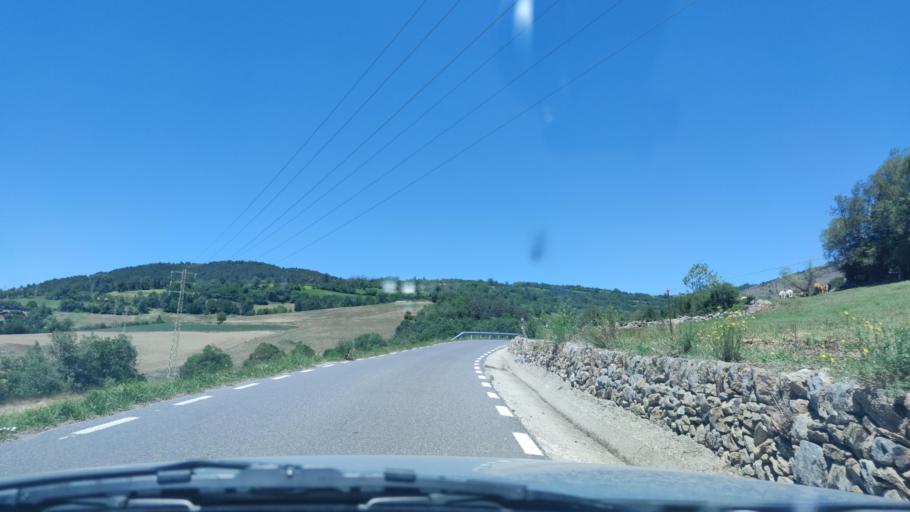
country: ES
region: Catalonia
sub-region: Provincia de Lleida
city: Bellver de Cerdanya
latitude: 42.3738
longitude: 1.7425
